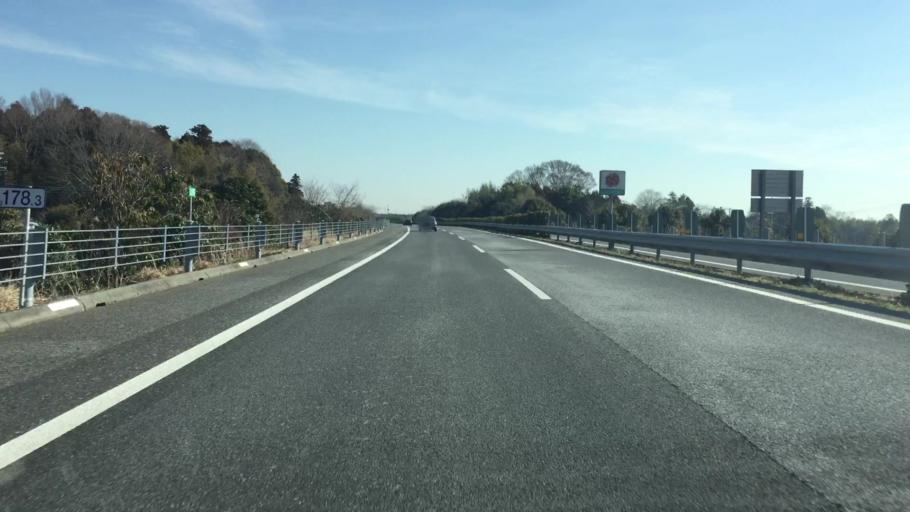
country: JP
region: Ibaraki
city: Mito-shi
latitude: 36.3177
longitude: 140.4702
